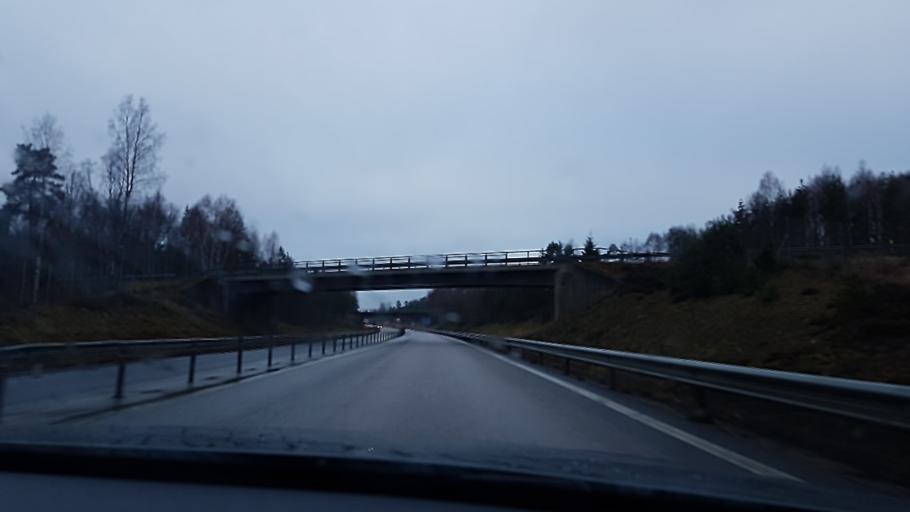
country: SE
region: Kronoberg
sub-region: Ljungby Kommun
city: Lagan
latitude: 56.9303
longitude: 13.9822
